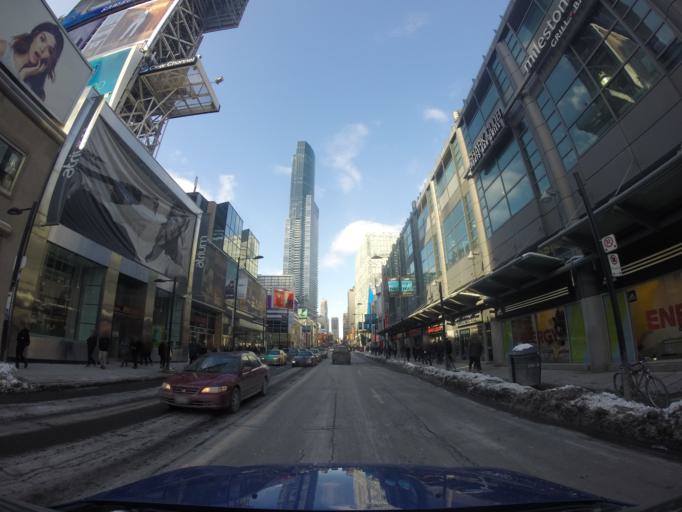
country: CA
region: Ontario
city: Toronto
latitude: 43.6564
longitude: -79.3810
